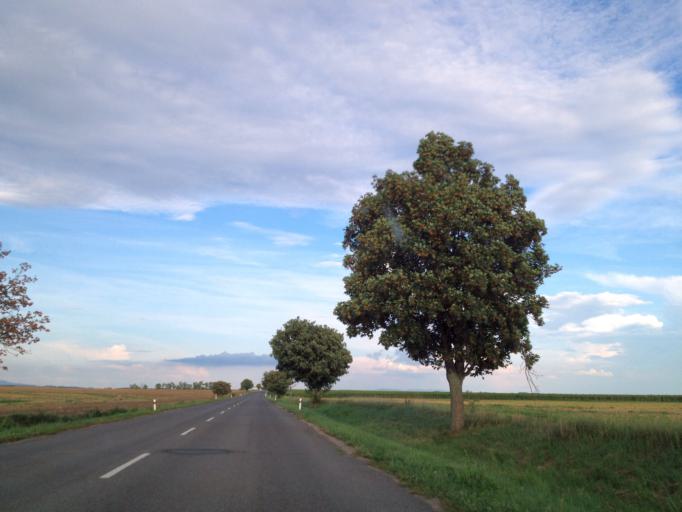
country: SK
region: Nitriansky
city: Svodin
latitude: 47.8961
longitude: 18.3806
